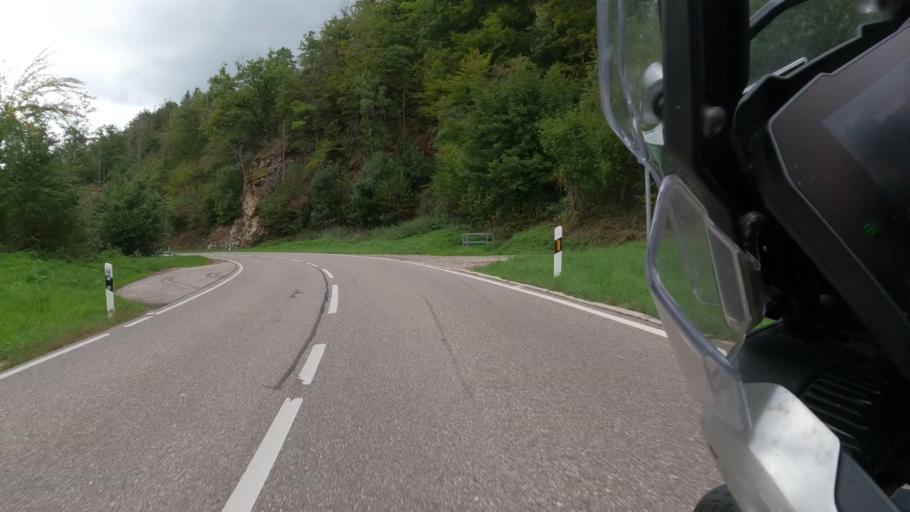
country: DE
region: Baden-Wuerttemberg
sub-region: Freiburg Region
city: Uhlingen-Birkendorf
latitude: 47.7116
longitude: 8.3455
